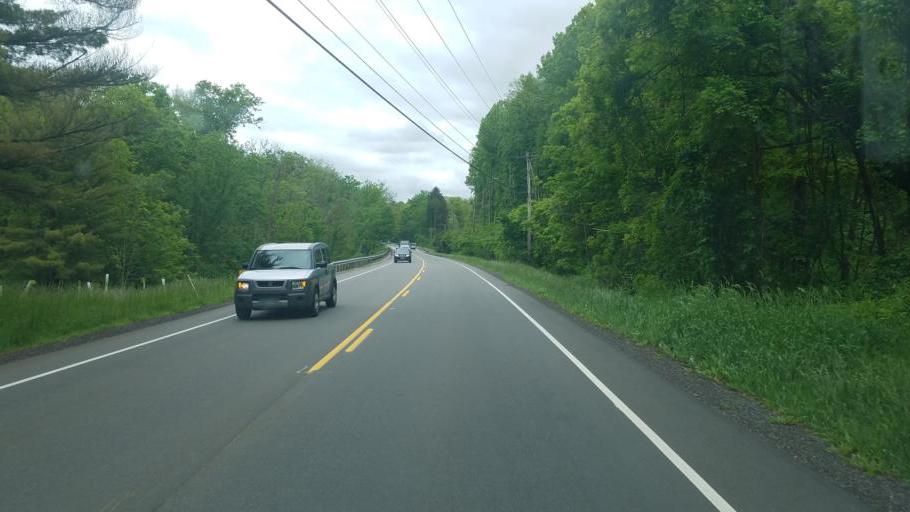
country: US
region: Ohio
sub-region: Summit County
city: Boston Heights
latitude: 41.2319
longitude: -81.5150
